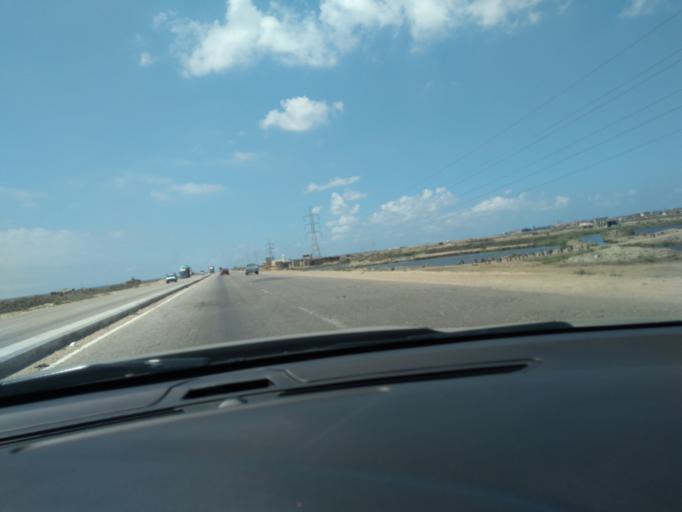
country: EG
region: Muhafazat ad Daqahliyah
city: Al Matariyah
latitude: 31.3195
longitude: 32.1120
